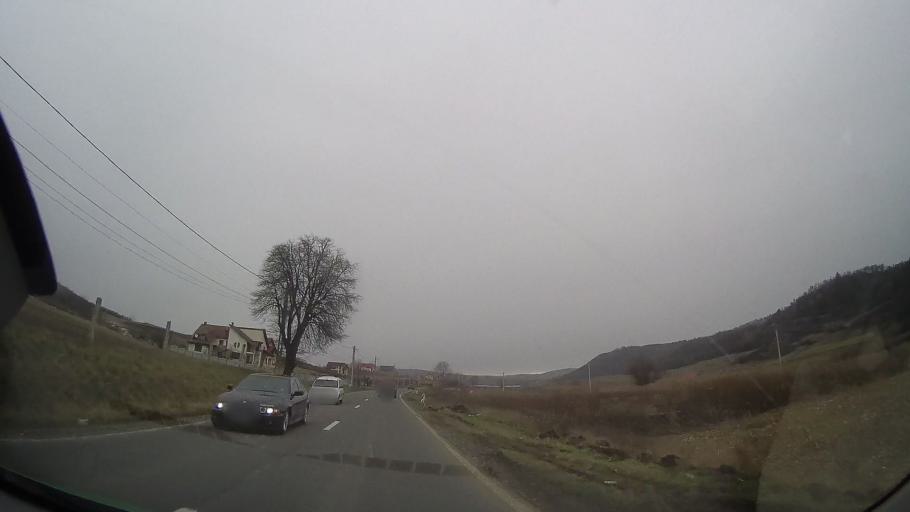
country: RO
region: Mures
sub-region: Comuna Ceausu de Campie
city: Ceausu de Campie
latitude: 46.6221
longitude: 24.5232
